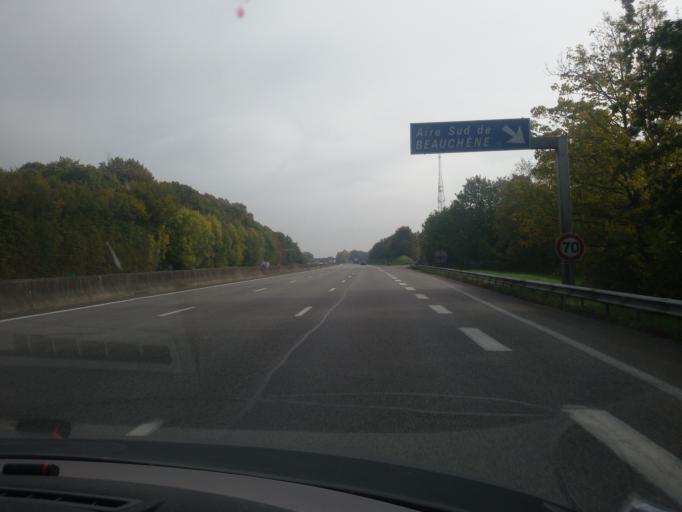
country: FR
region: Haute-Normandie
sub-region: Departement de l'Eure
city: Houlbec-Cocherel
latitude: 49.1072
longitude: 1.3422
